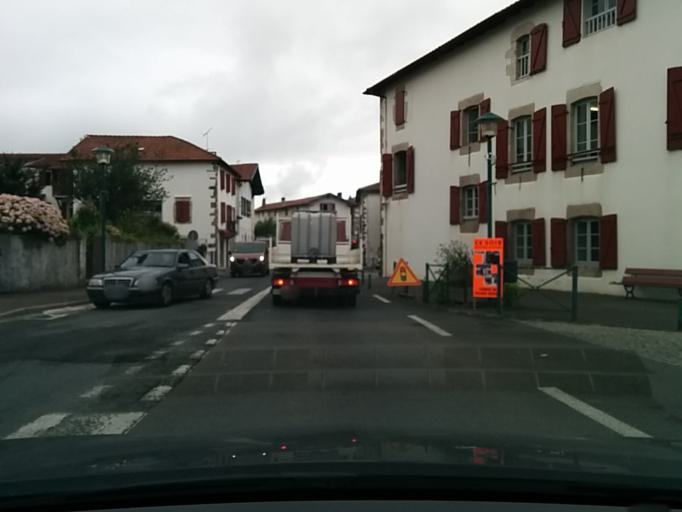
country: FR
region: Aquitaine
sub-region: Departement des Pyrenees-Atlantiques
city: Saint-Pee-sur-Nivelle
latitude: 43.3568
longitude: -1.5514
